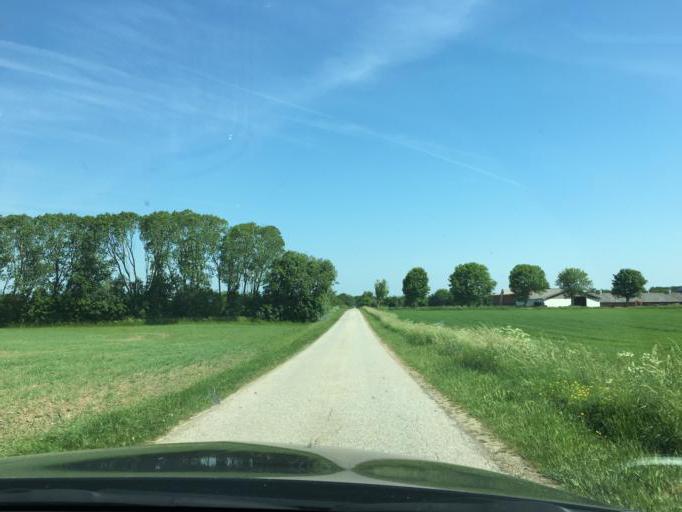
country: DK
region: South Denmark
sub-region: Kolding Kommune
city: Kolding
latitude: 55.5571
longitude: 9.4759
